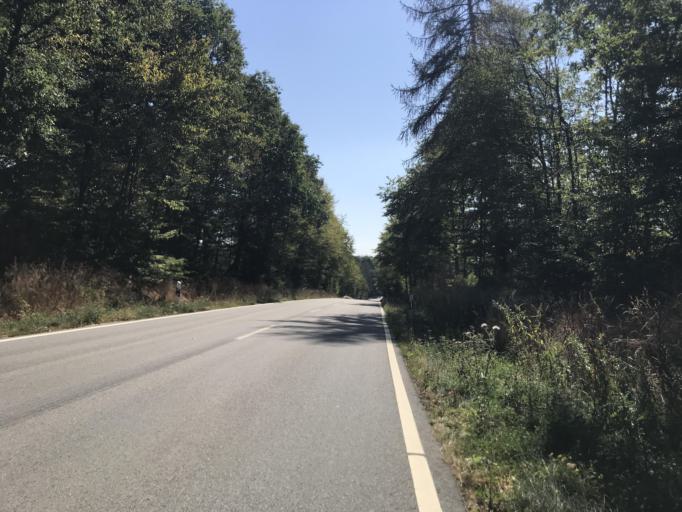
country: DE
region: Rheinland-Pfalz
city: Trechtingshausen
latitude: 50.0578
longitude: 7.9118
